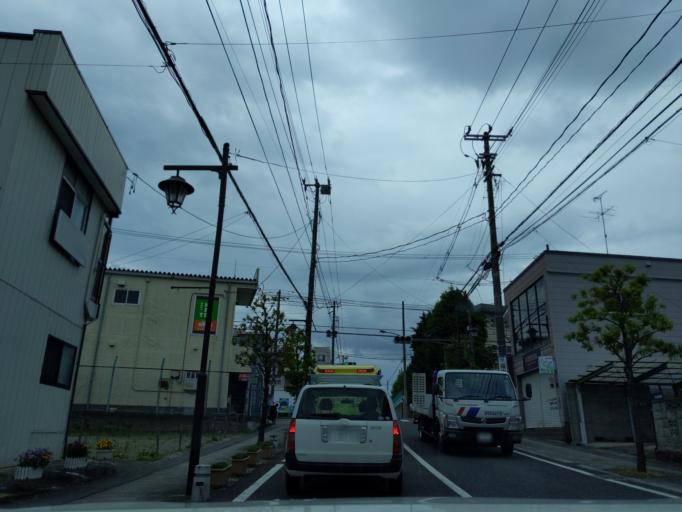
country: JP
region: Fukushima
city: Koriyama
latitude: 37.3870
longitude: 140.3708
